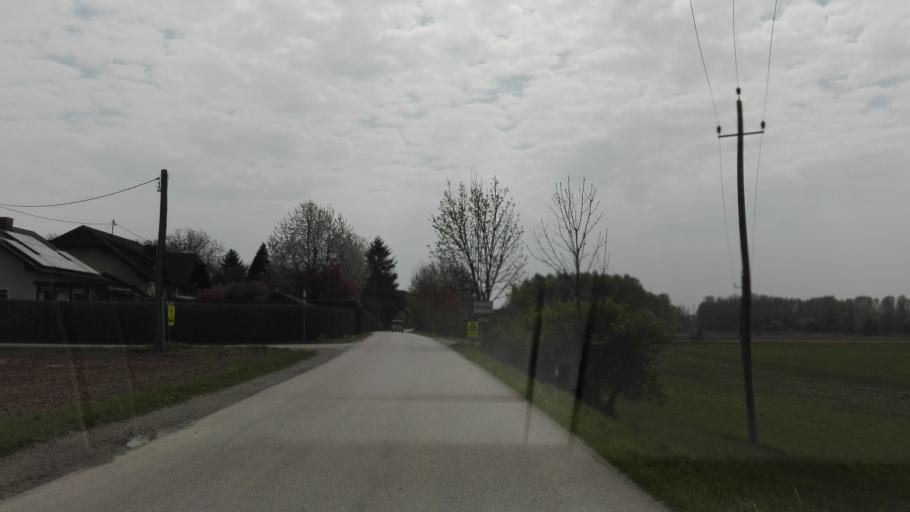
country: AT
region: Upper Austria
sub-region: Politischer Bezirk Perg
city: Perg
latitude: 48.2402
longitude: 14.5984
